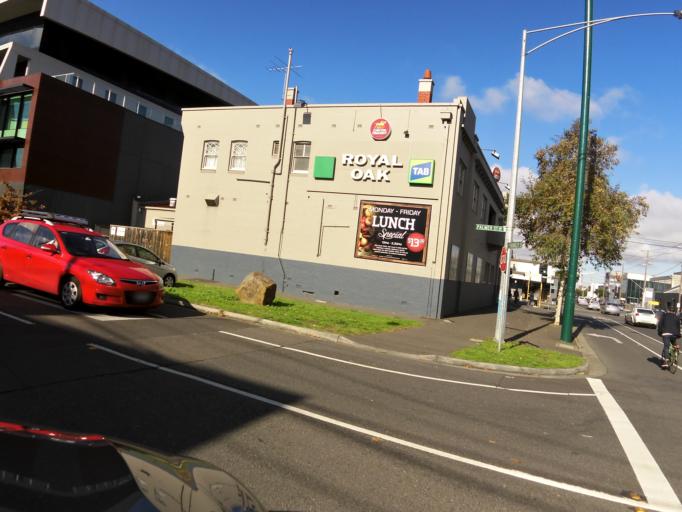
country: AU
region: Victoria
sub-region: Yarra
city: Richmond
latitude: -37.8189
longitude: 145.0085
